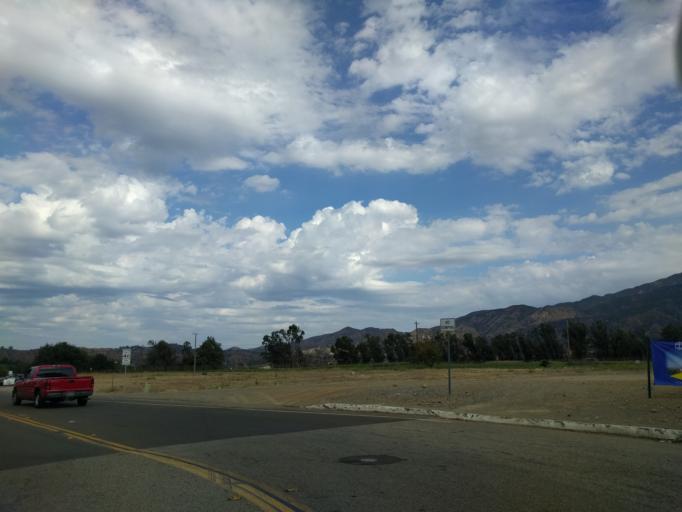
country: US
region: California
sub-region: Orange County
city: Trabuco Canyon
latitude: 33.6566
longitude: -117.5765
